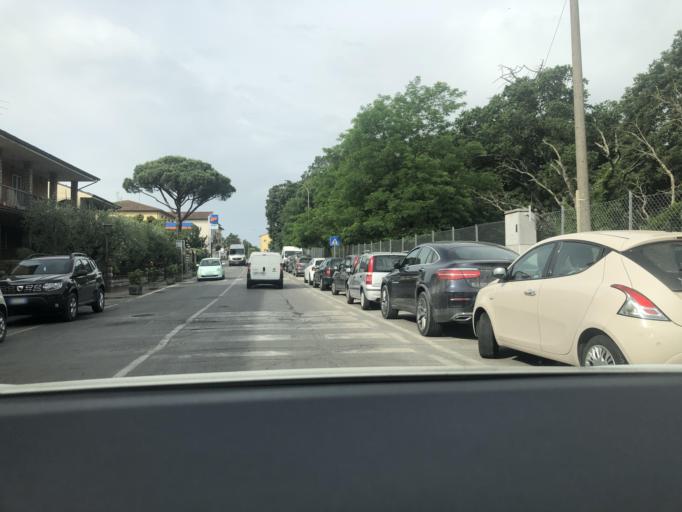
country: IT
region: Tuscany
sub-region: Provincia di Pistoia
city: Lamporecchio
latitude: 43.8146
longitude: 10.8936
